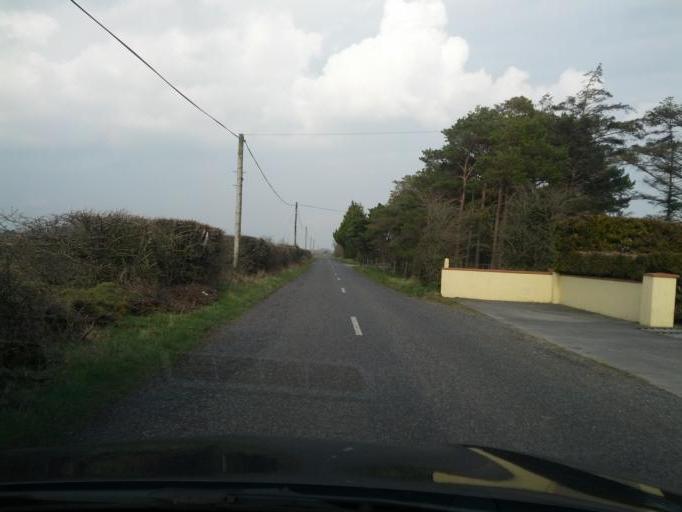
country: IE
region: Connaught
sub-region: County Galway
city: Athenry
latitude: 53.4346
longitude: -8.5682
